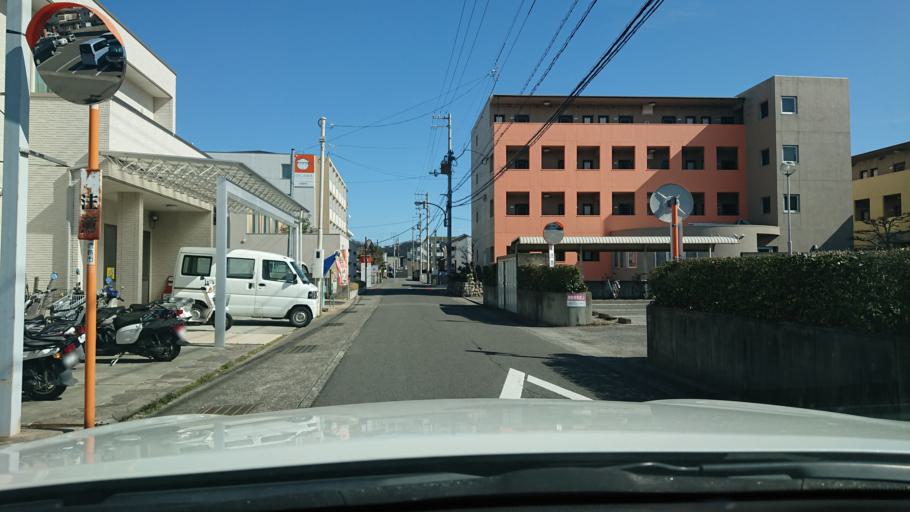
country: JP
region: Tokushima
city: Tokushima-shi
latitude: 34.0510
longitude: 134.5562
